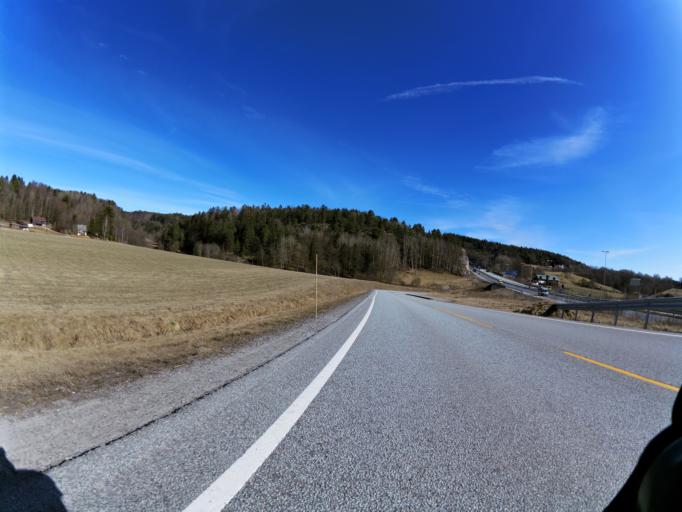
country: NO
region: Ostfold
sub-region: Fredrikstad
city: Fredrikstad
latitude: 59.3171
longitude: 10.9873
